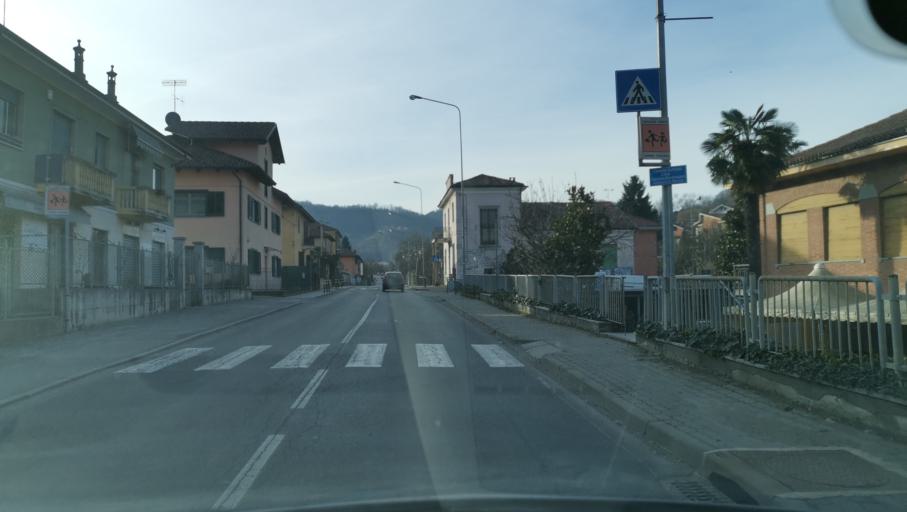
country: IT
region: Piedmont
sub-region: Provincia di Torino
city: Castiglione Torinese
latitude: 45.1145
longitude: 7.8164
